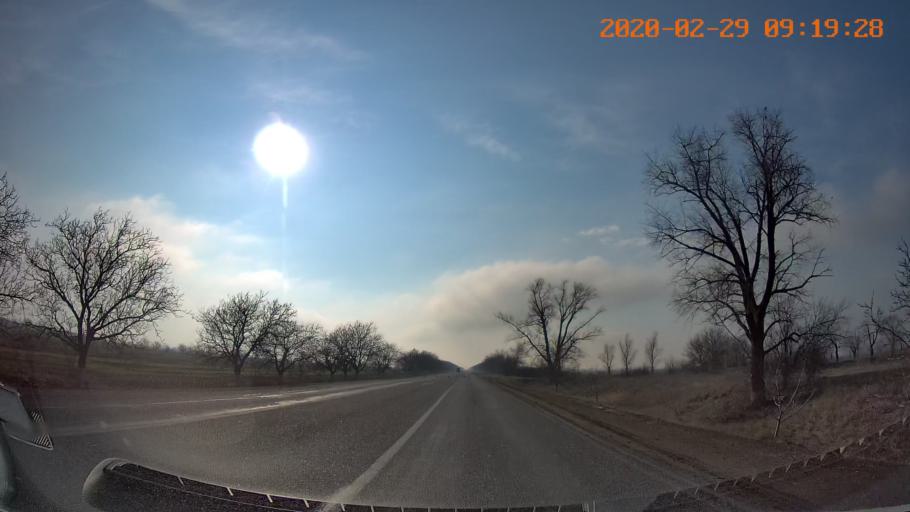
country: MD
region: Telenesti
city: Pervomaisc
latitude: 46.7623
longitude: 29.9394
